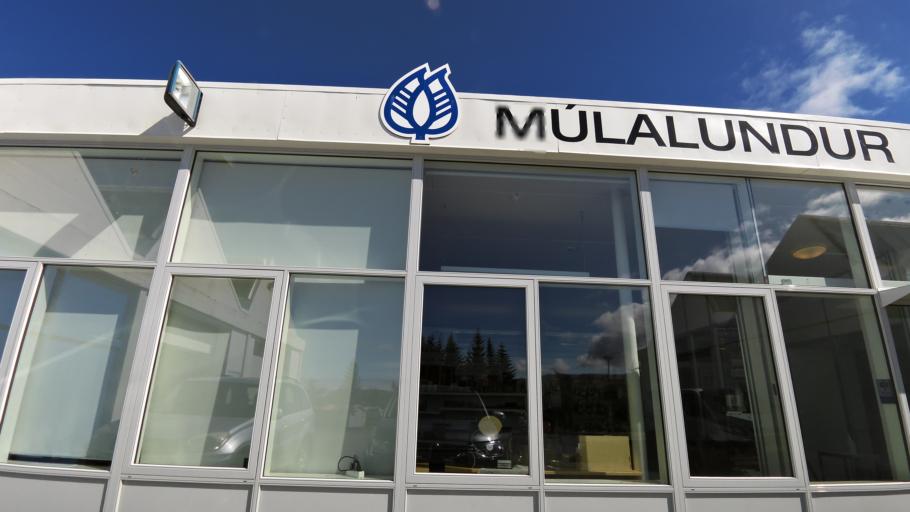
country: IS
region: Capital Region
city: Mosfellsbaer
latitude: 64.1641
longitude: -21.6633
